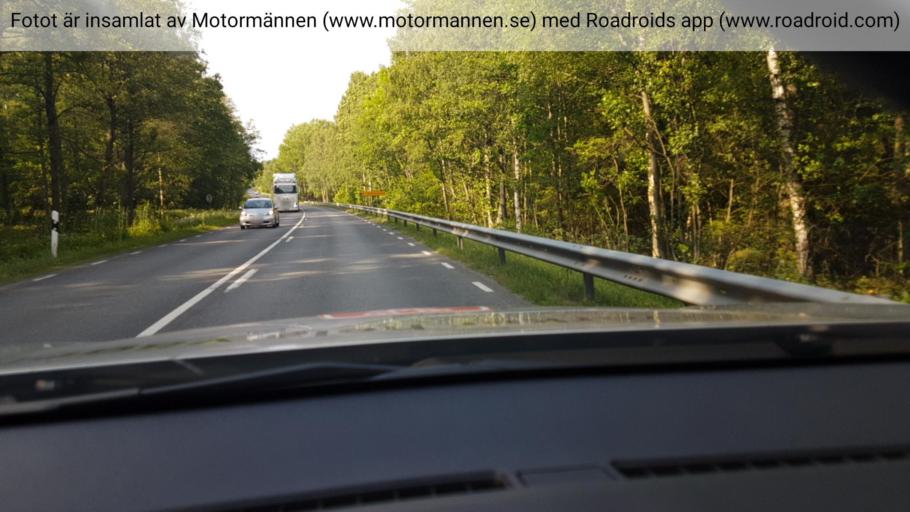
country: SE
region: Vaestra Goetaland
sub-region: Hjo Kommun
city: Hjo
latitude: 58.0997
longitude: 14.2076
